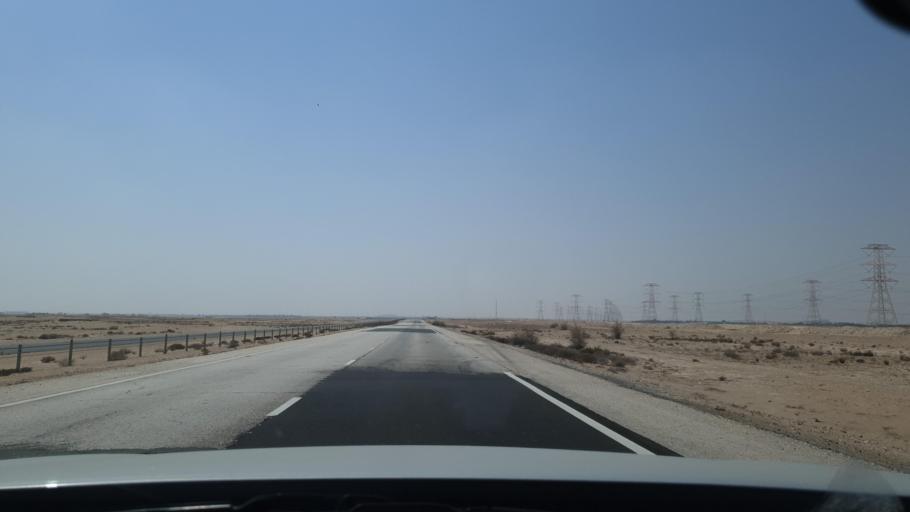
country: QA
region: Al Khawr
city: Al Khawr
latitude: 25.7079
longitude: 51.4464
